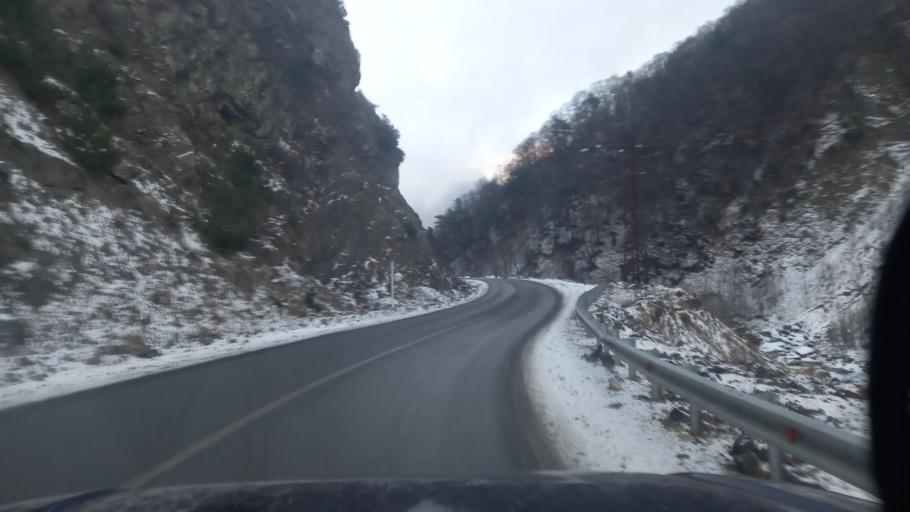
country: RU
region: Ingushetiya
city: Dzhayrakh
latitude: 42.7907
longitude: 44.7735
